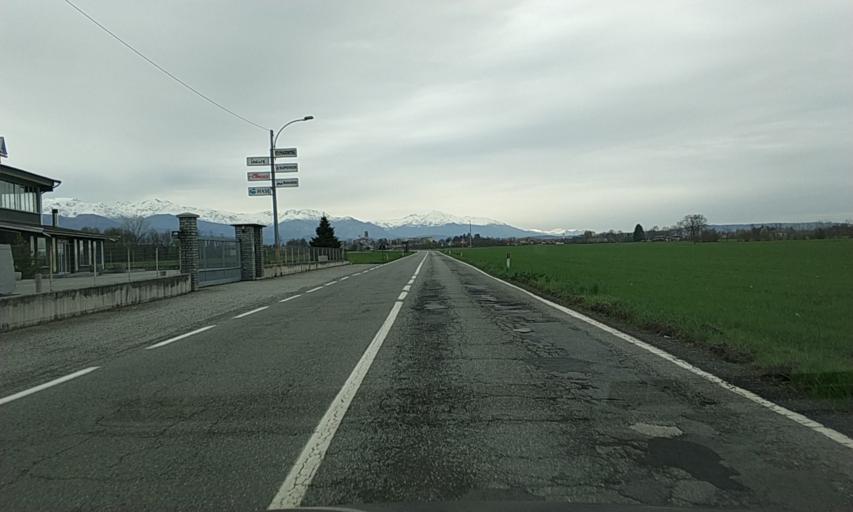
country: IT
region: Piedmont
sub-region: Provincia di Torino
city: Favria
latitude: 45.3176
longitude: 7.6813
